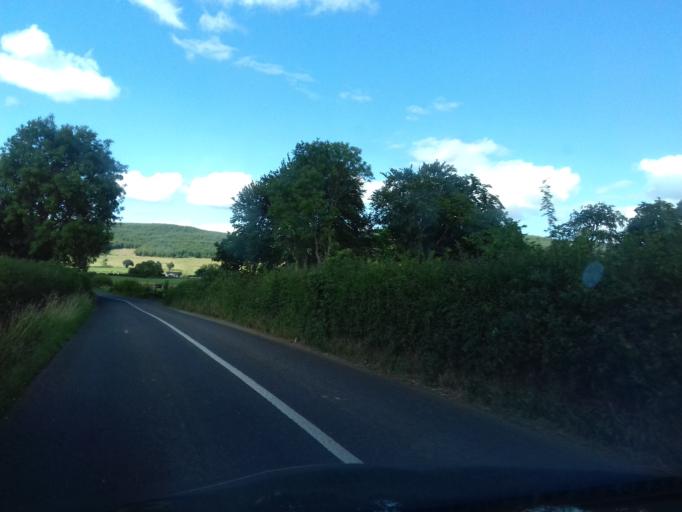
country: IE
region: Munster
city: Carrick-on-Suir
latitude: 52.3895
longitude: -7.4677
